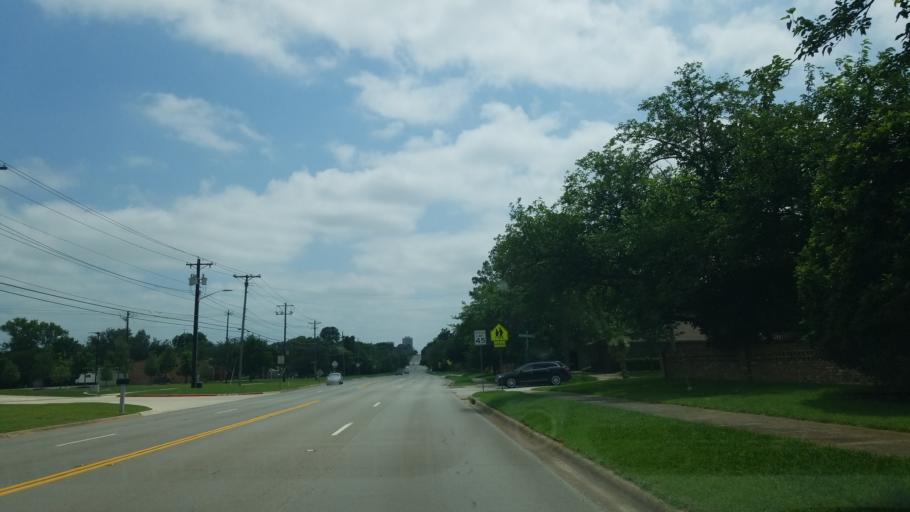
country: US
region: Texas
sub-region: Denton County
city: Denton
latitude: 33.2506
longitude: -97.1148
